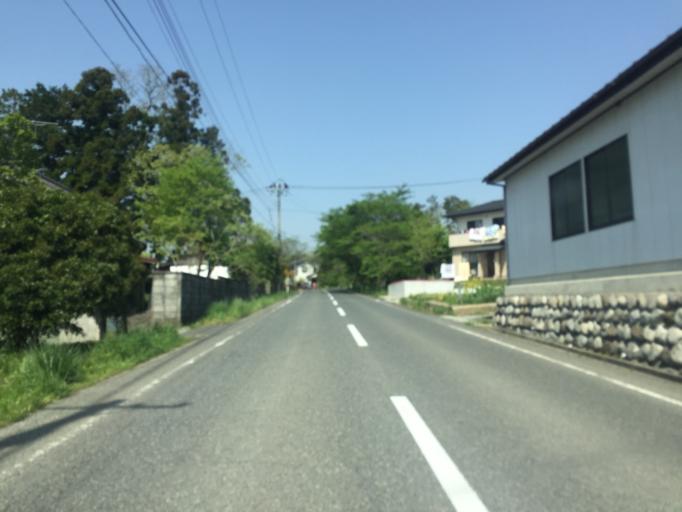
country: JP
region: Miyagi
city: Marumori
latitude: 37.7717
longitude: 140.9397
